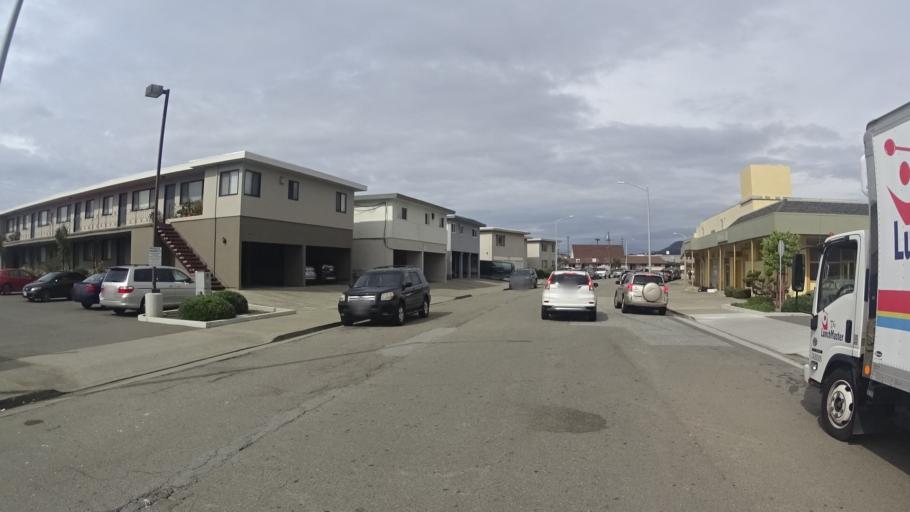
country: US
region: California
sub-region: San Mateo County
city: South San Francisco
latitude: 37.6486
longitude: -122.4304
